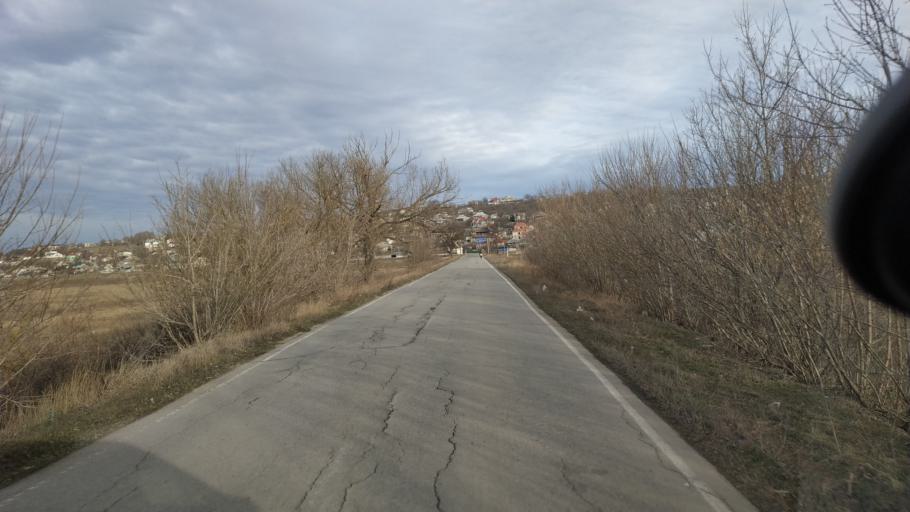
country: MD
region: Chisinau
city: Vadul lui Voda
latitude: 47.1134
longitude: 29.0587
